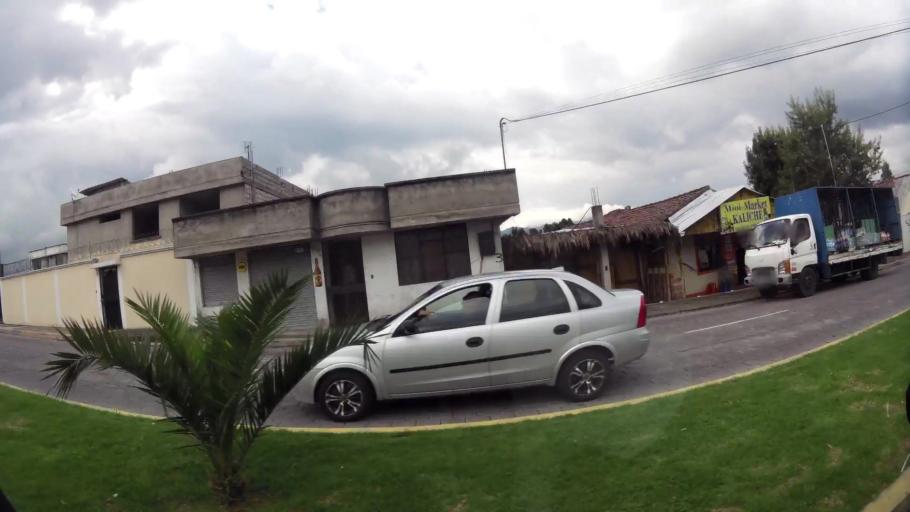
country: EC
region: Pichincha
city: Sangolqui
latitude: -0.3293
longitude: -78.4563
